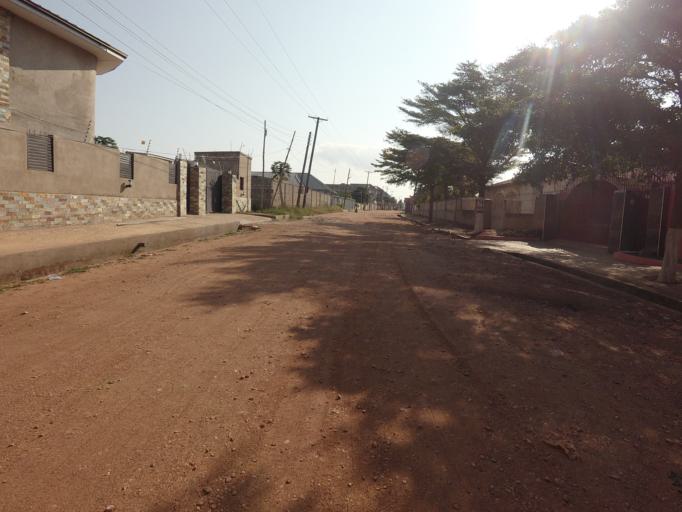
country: GH
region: Greater Accra
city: Nungua
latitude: 5.6365
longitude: -0.0855
